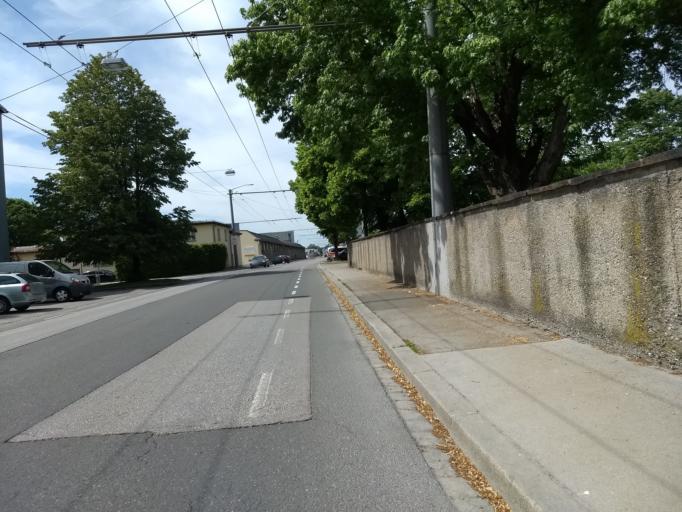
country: AT
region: Salzburg
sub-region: Salzburg Stadt
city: Salzburg
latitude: 47.8043
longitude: 13.0142
